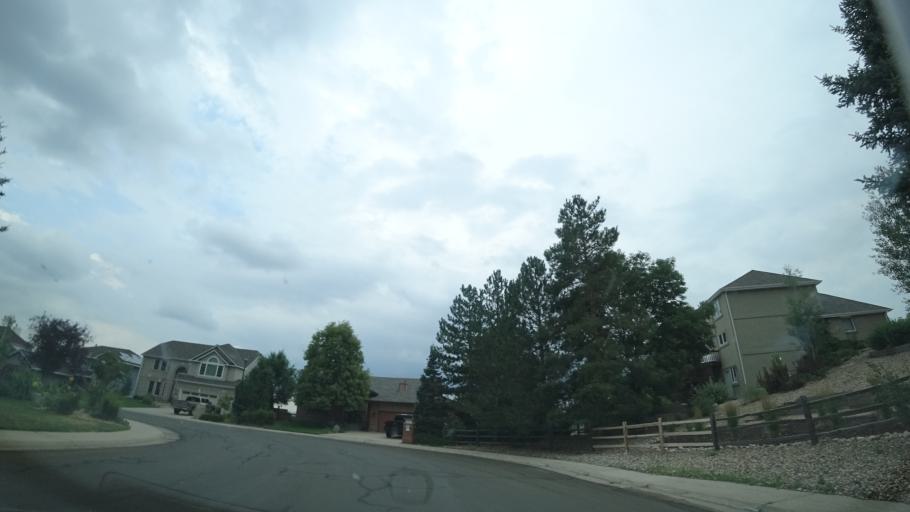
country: US
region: Colorado
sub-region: Jefferson County
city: West Pleasant View
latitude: 39.7087
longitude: -105.1447
